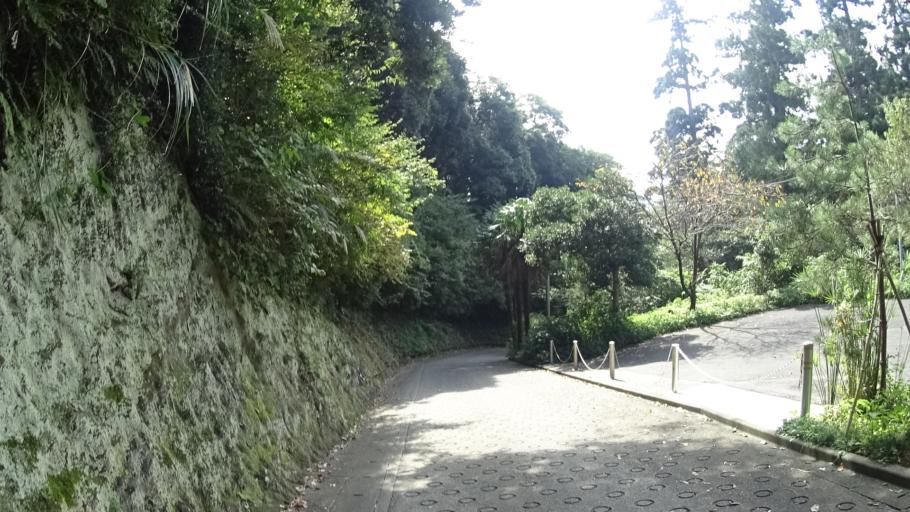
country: JP
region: Kanagawa
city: Zushi
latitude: 35.3034
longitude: 139.6065
